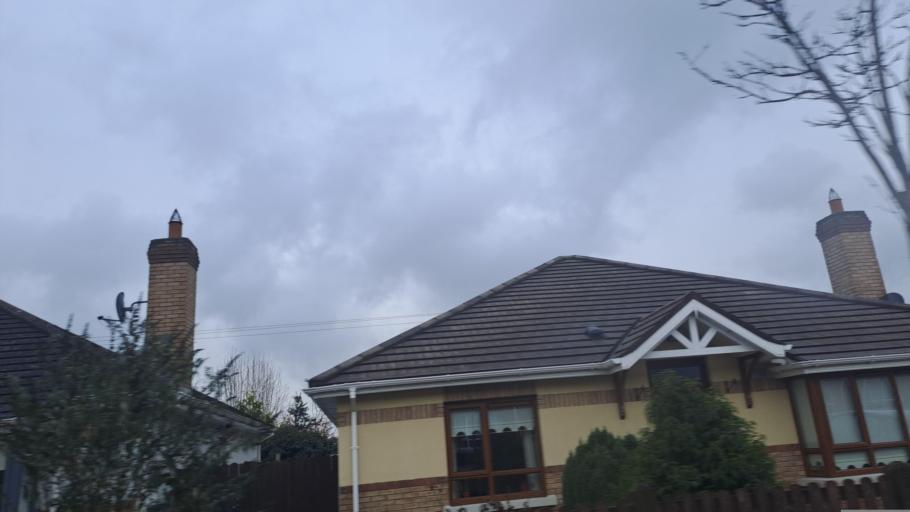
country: IE
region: Ulster
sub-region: An Cabhan
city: Virginia
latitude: 53.8386
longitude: -7.0788
